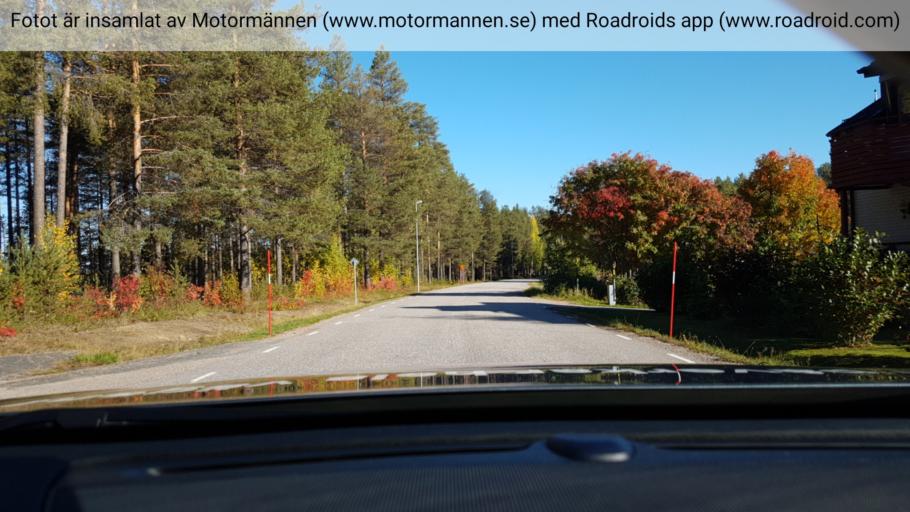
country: SE
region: Norrbotten
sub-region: Gallivare Kommun
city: Gaellivare
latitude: 66.4350
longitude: 20.6087
